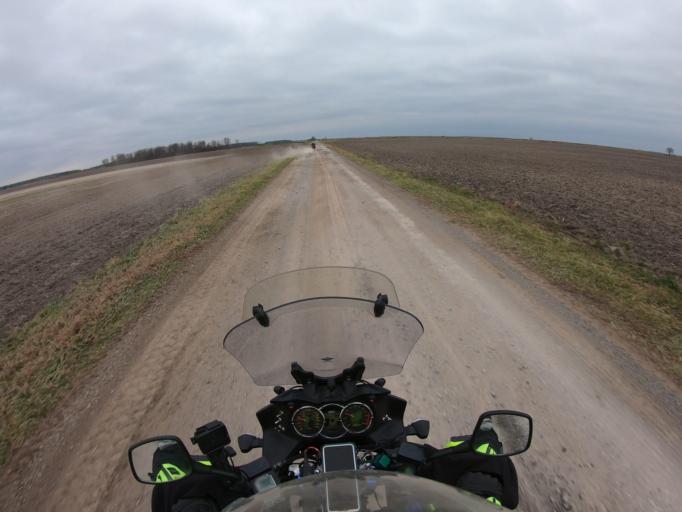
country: US
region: Michigan
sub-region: Saginaw County
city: Burt
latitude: 43.2640
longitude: -83.9851
